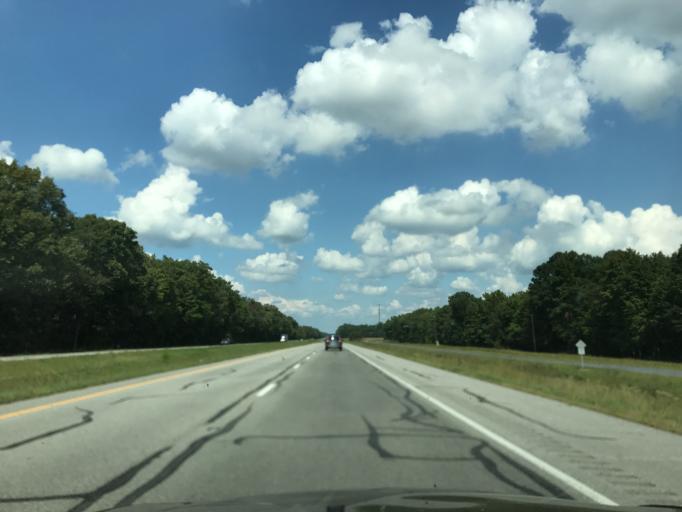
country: US
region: Delaware
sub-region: New Castle County
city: Townsend
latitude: 39.2875
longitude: -75.8548
